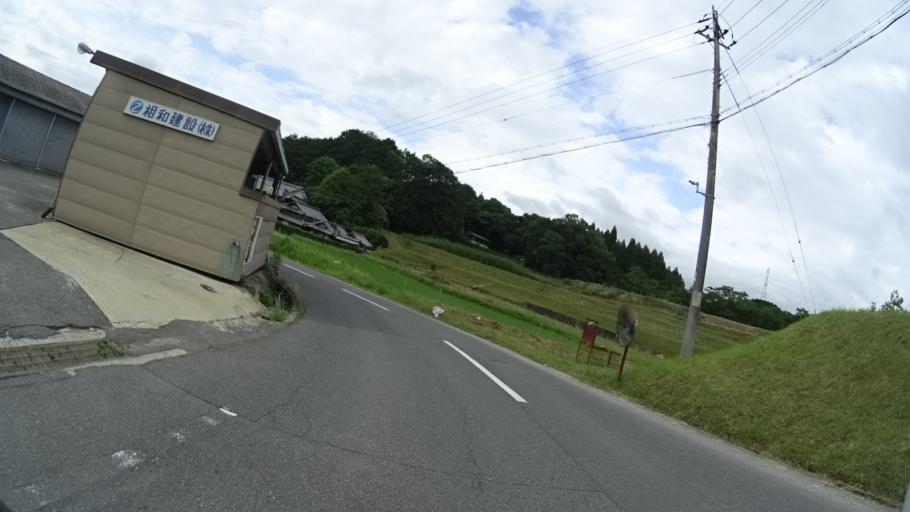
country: JP
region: Nara
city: Nara-shi
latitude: 34.7196
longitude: 135.9106
